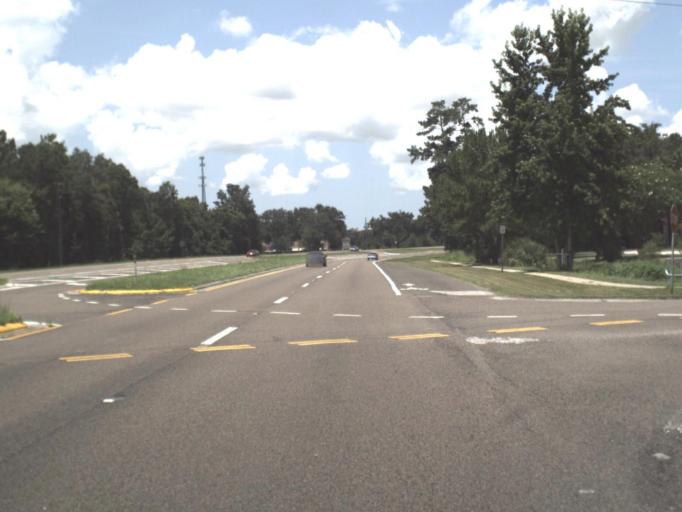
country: US
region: Florida
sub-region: Hernando County
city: South Brooksville
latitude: 28.5435
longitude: -82.4151
